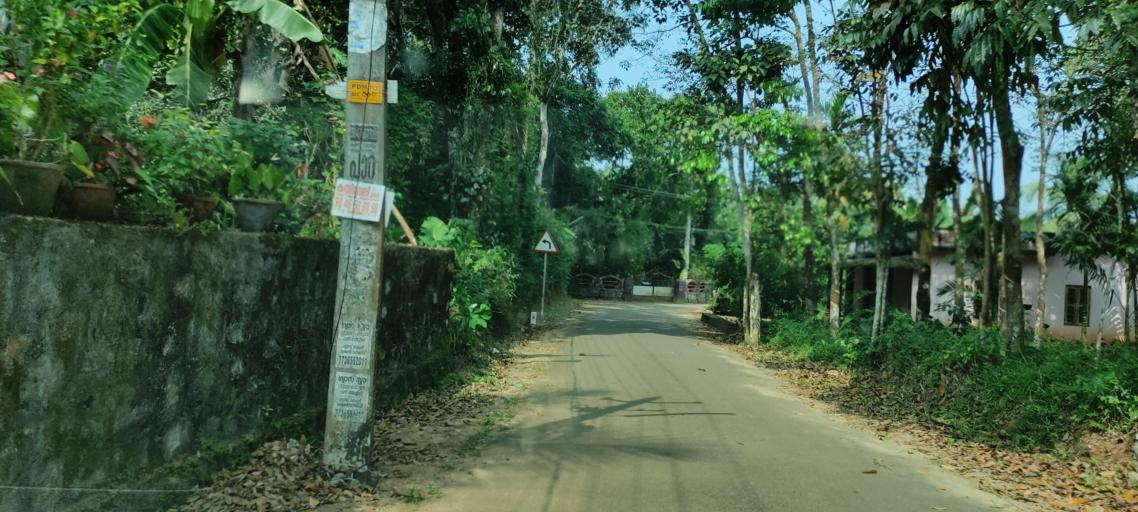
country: IN
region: Kerala
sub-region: Pattanamtitta
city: Adur
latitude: 9.2065
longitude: 76.6927
